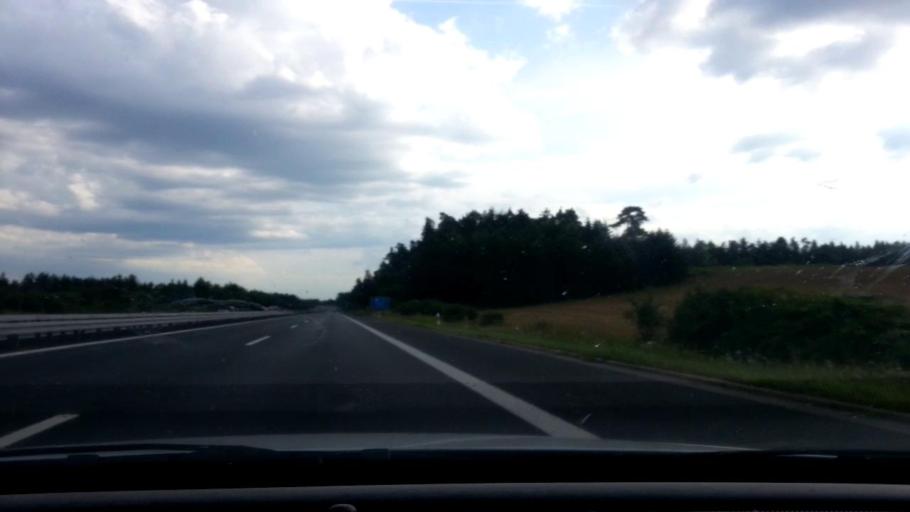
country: DE
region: Bavaria
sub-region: Upper Palatinate
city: Mitterteich
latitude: 49.9241
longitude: 12.2245
